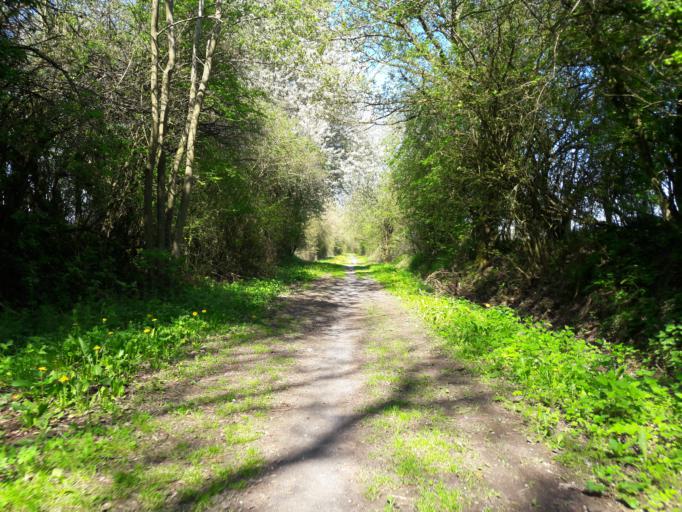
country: FR
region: Nord-Pas-de-Calais
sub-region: Departement du Nord
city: Sains-du-Nord
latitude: 50.1666
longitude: 4.0743
